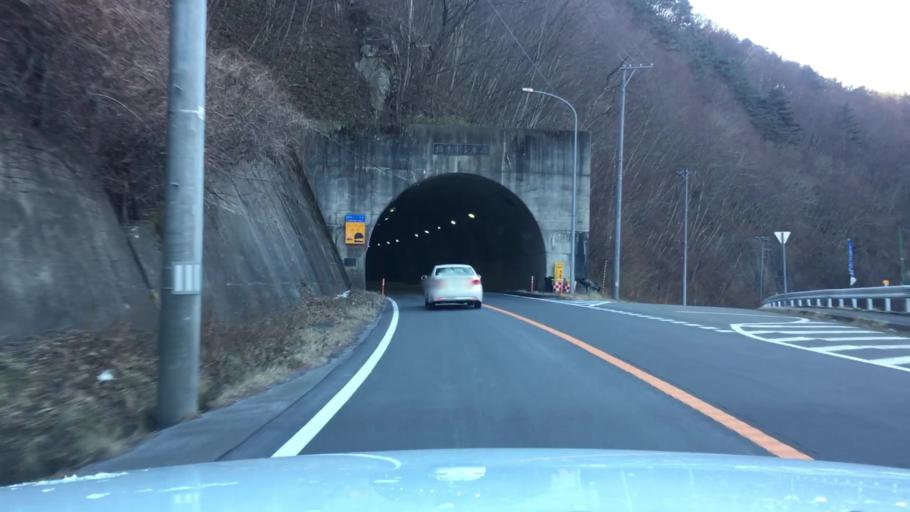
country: JP
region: Iwate
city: Tono
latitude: 39.6382
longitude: 141.6004
